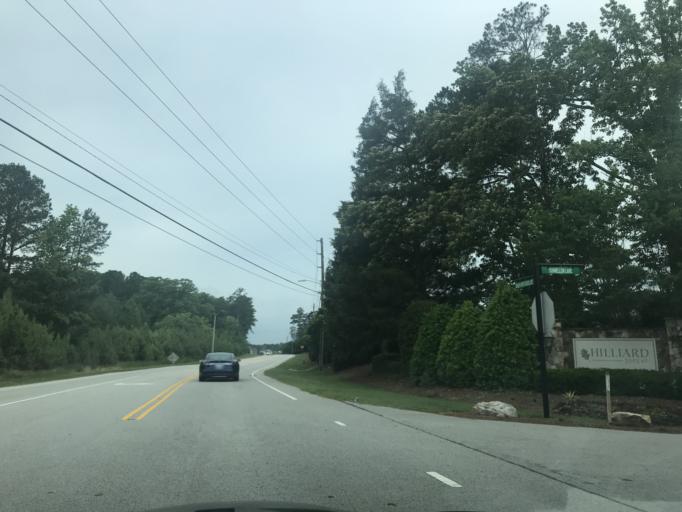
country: US
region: North Carolina
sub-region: Wake County
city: Green Level
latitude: 35.7999
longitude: -78.8967
